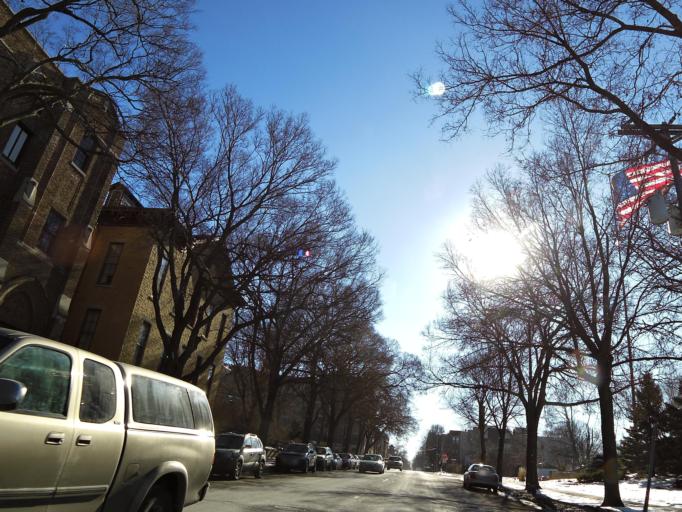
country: US
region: Minnesota
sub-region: Ramsey County
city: Saint Paul
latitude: 44.9492
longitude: -93.1162
